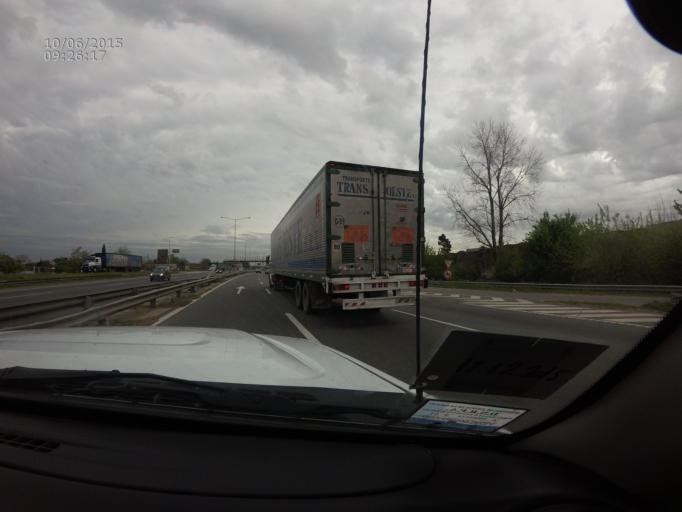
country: AR
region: Buenos Aires
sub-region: Partido de Campana
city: Campana
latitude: -34.1770
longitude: -58.9738
